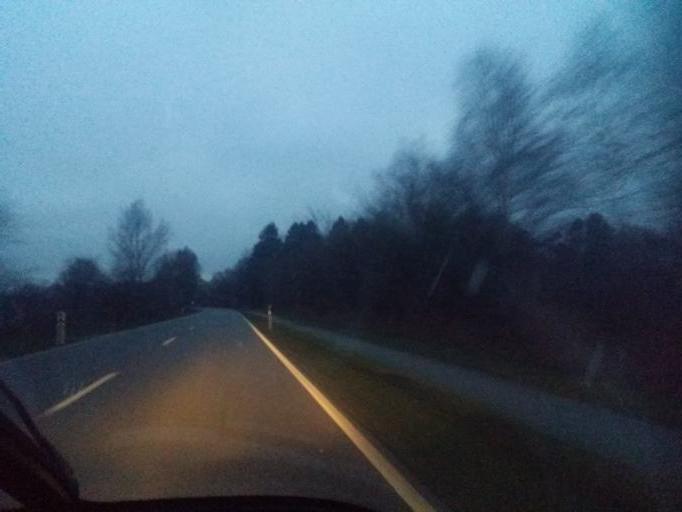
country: DE
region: Schleswig-Holstein
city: Kaisborstel
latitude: 54.0263
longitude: 9.4762
